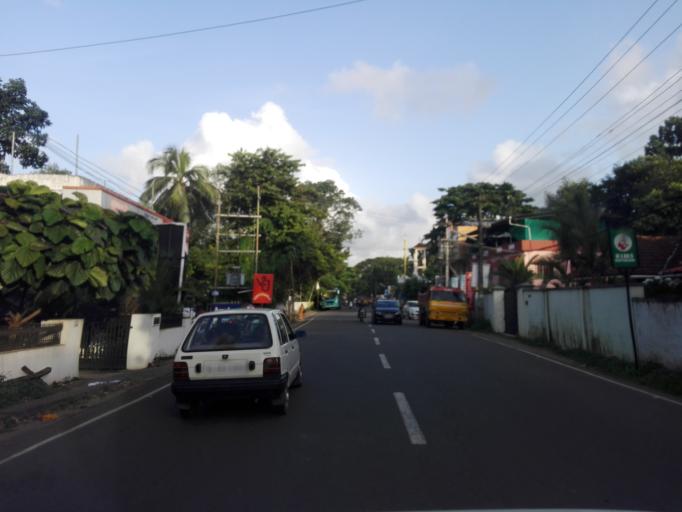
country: IN
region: Kerala
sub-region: Kottayam
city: Kottayam
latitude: 9.6037
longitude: 76.5162
